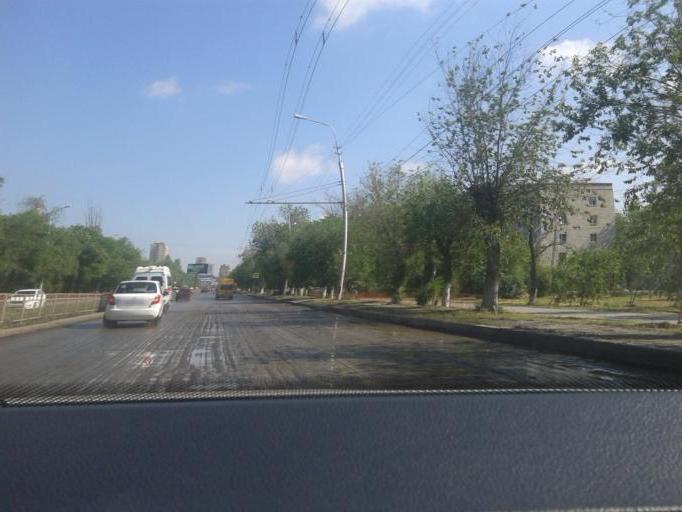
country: RU
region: Volgograd
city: Volgograd
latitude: 48.6086
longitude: 44.4224
